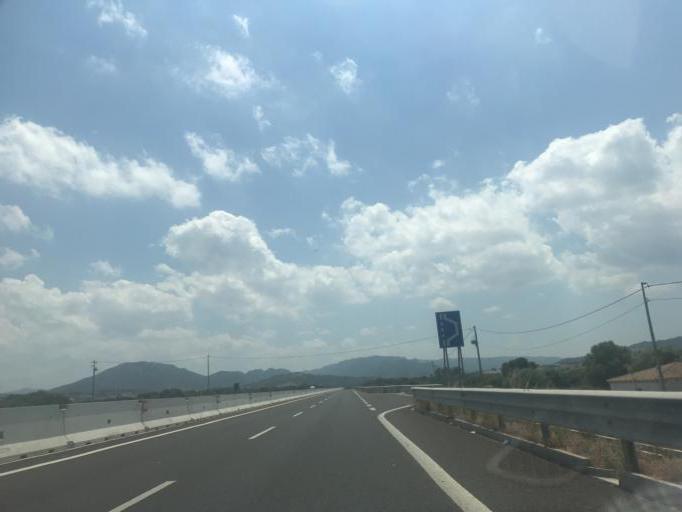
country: IT
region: Sardinia
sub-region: Provincia di Olbia-Tempio
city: Loiri Porto San Paolo
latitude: 40.8757
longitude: 9.4623
